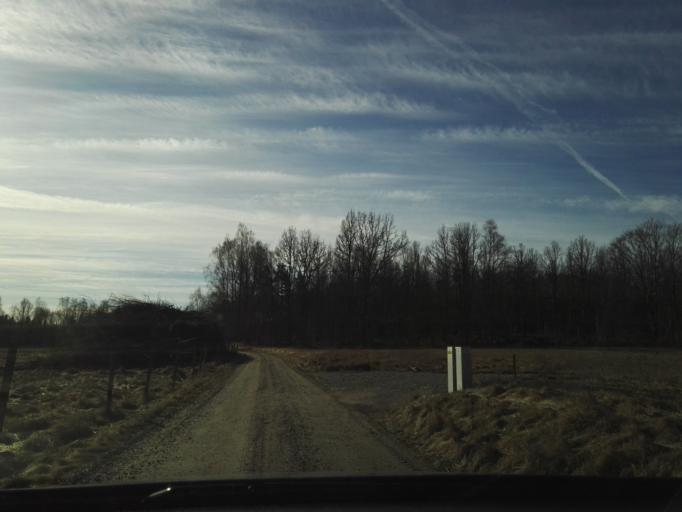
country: SE
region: Kronoberg
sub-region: Vaxjo Kommun
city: Vaexjoe
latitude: 56.9307
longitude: 14.7487
